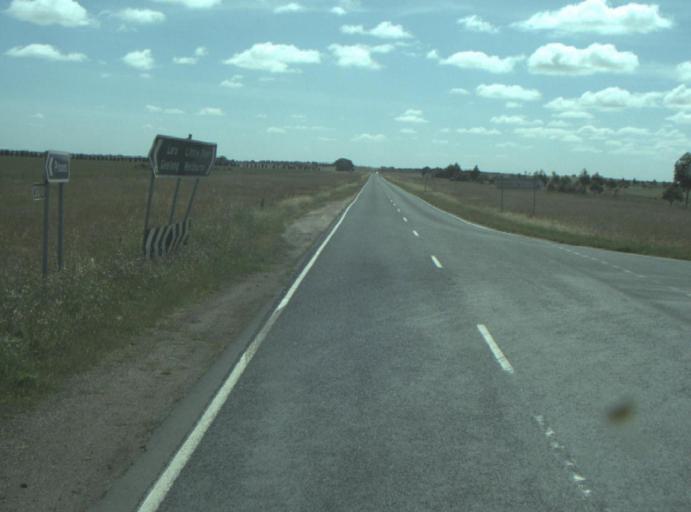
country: AU
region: Victoria
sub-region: Wyndham
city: Little River
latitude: -38.0079
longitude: 144.4621
